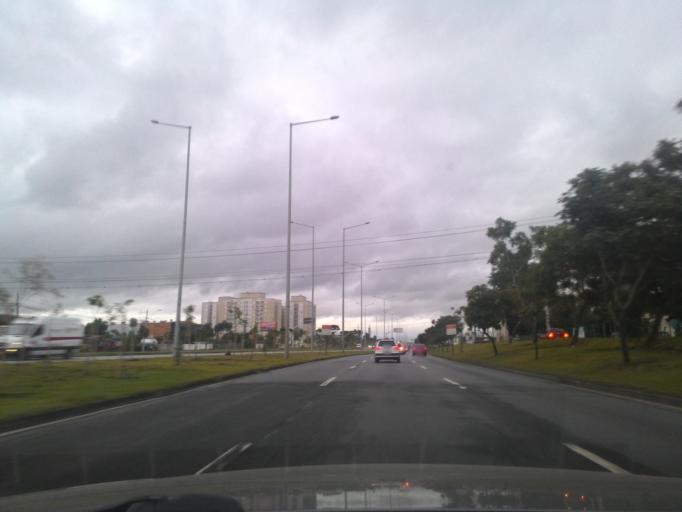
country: BR
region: Parana
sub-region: Curitiba
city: Curitiba
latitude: -25.4952
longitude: -49.2747
